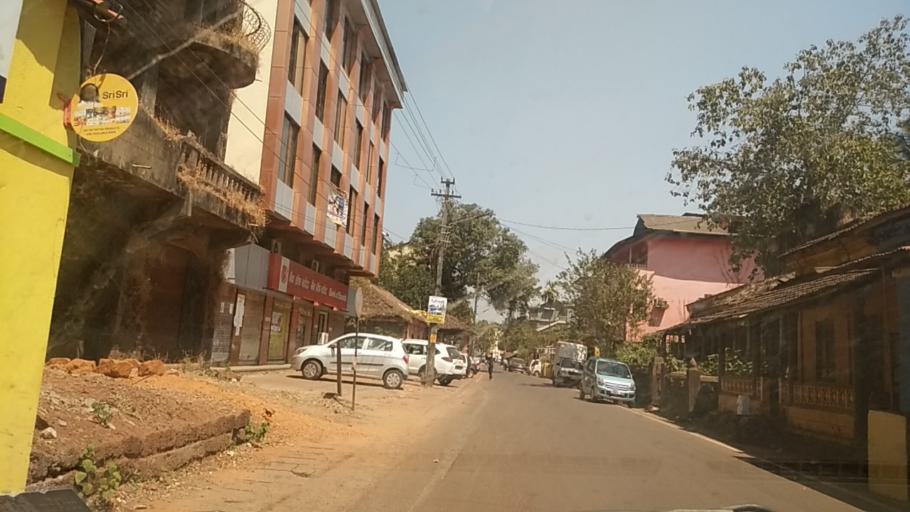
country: IN
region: Goa
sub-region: North Goa
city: Dicholi
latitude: 15.5886
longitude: 73.9448
